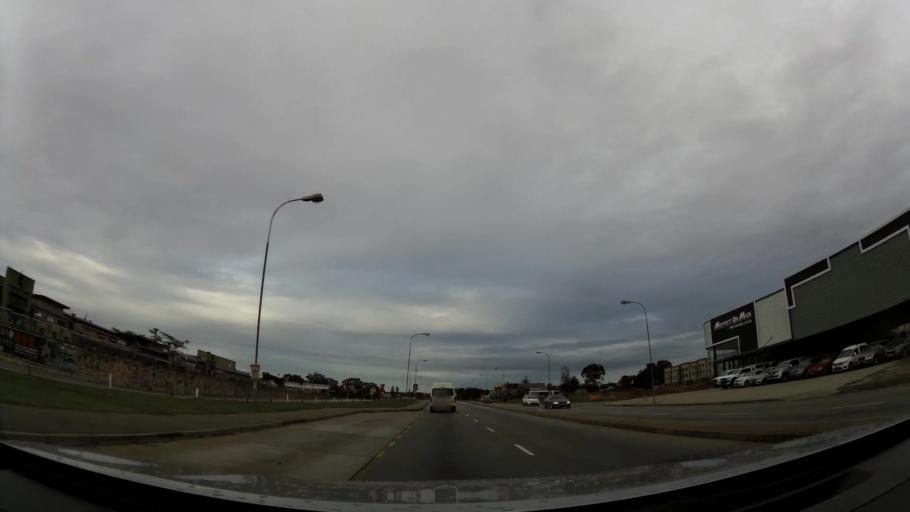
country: ZA
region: Eastern Cape
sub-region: Nelson Mandela Bay Metropolitan Municipality
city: Port Elizabeth
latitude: -33.9821
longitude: 25.5532
